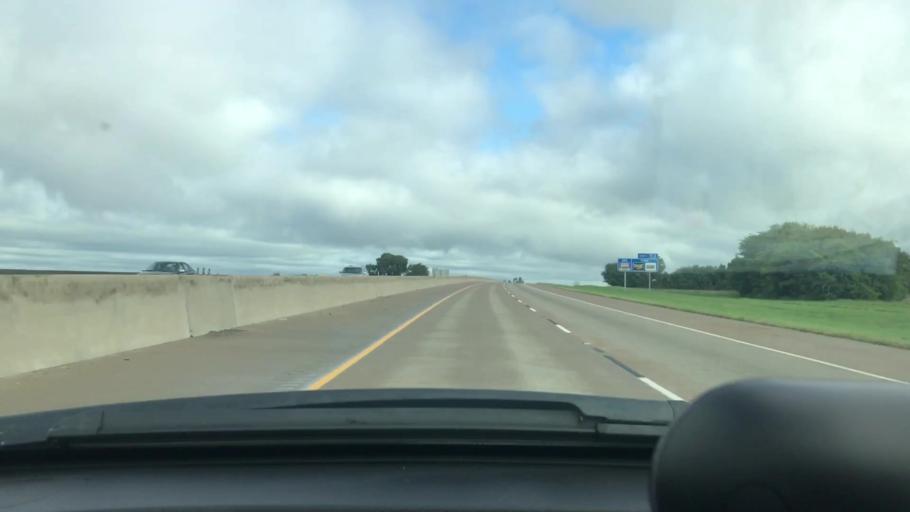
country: US
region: Texas
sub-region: Grayson County
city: Howe
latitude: 33.4768
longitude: -96.6186
